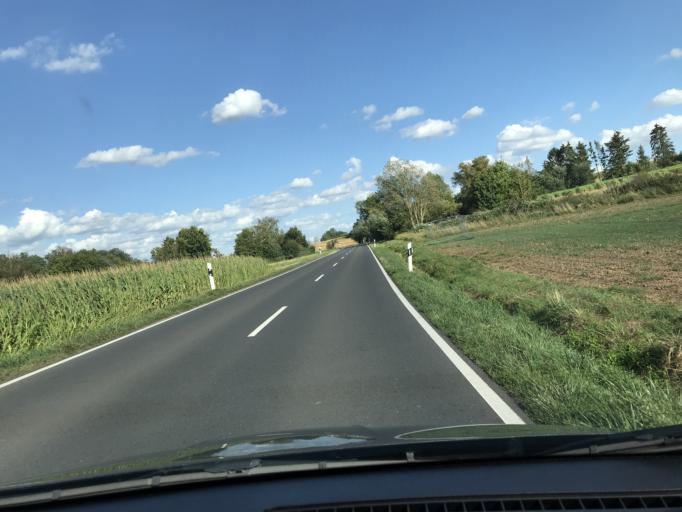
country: DE
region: Hesse
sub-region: Regierungsbezirk Darmstadt
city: Schaafheim
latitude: 49.9189
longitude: 8.9882
